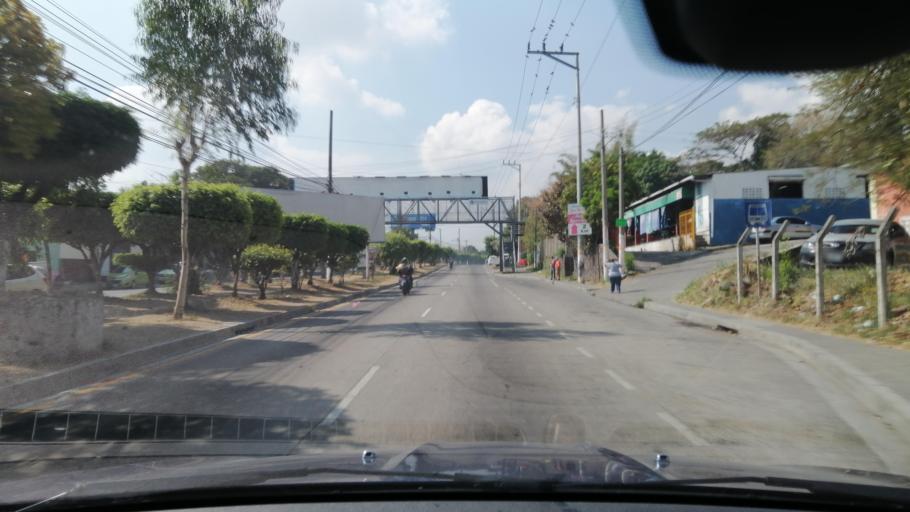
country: SV
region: San Salvador
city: Mejicanos
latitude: 13.7339
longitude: -89.2181
